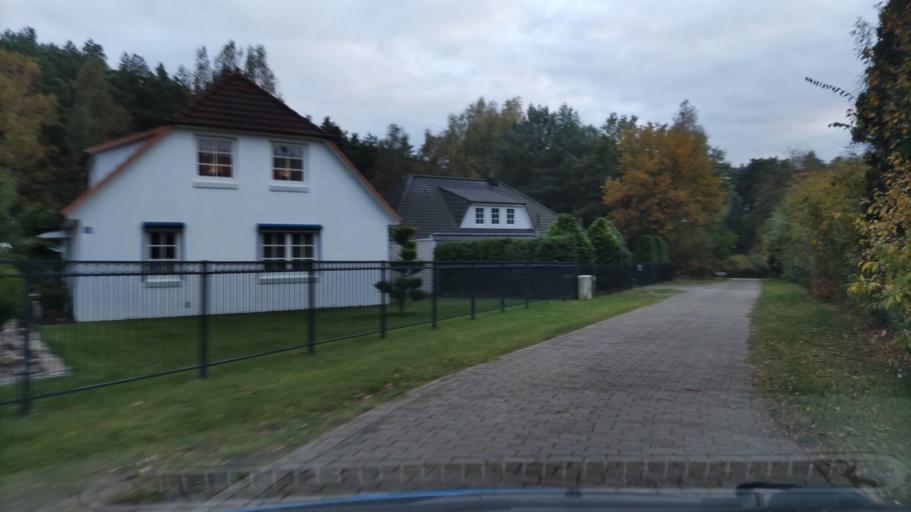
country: DE
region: Lower Saxony
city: Hitzacker
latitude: 53.1277
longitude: 11.0224
